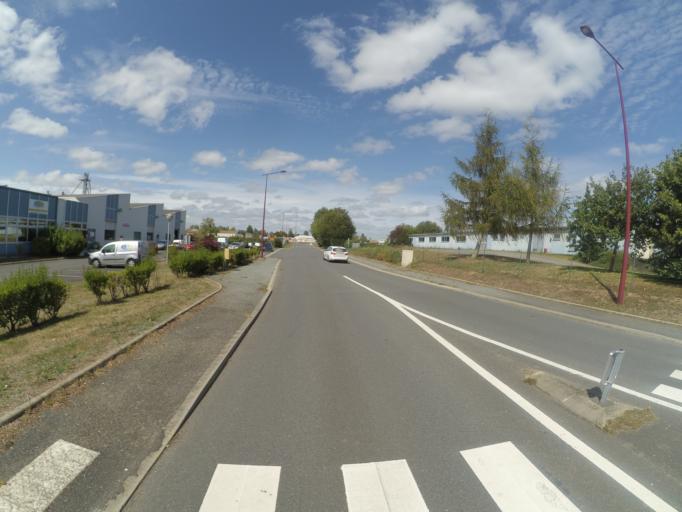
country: FR
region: Pays de la Loire
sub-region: Departement de la Loire-Atlantique
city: Clisson
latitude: 47.0778
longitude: -1.2900
